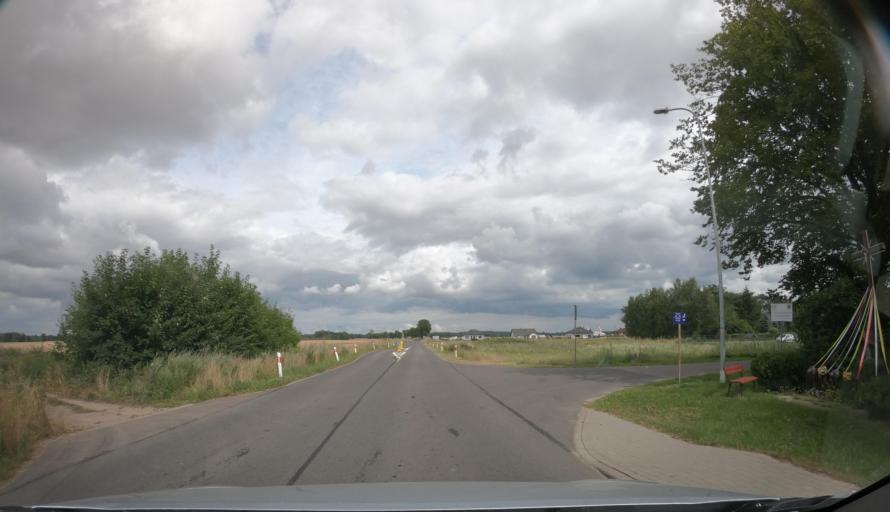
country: PL
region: West Pomeranian Voivodeship
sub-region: Koszalin
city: Koszalin
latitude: 54.1433
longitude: 16.0830
